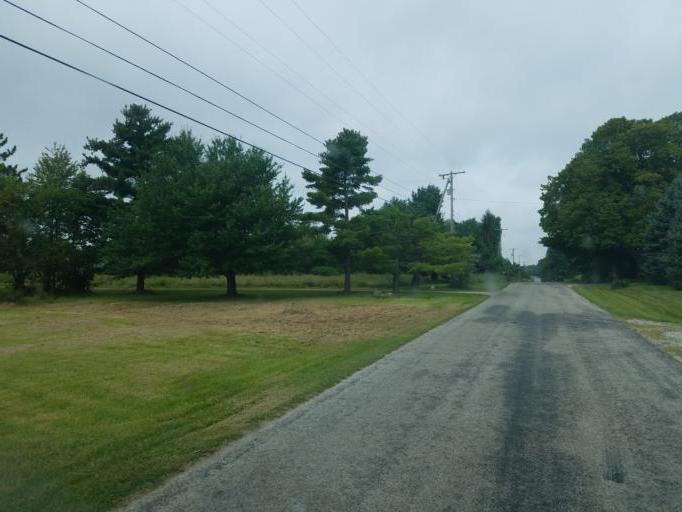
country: US
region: Ohio
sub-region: Morrow County
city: Cardington
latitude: 40.4158
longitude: -82.8374
